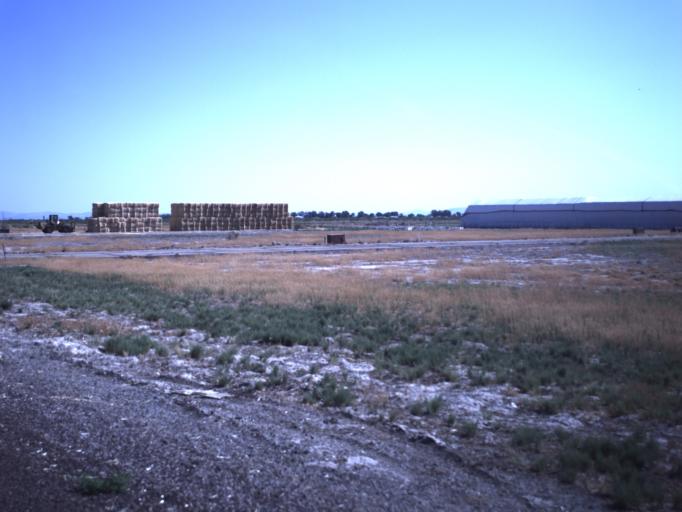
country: US
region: Utah
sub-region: Millard County
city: Delta
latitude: 39.3322
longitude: -112.6522
